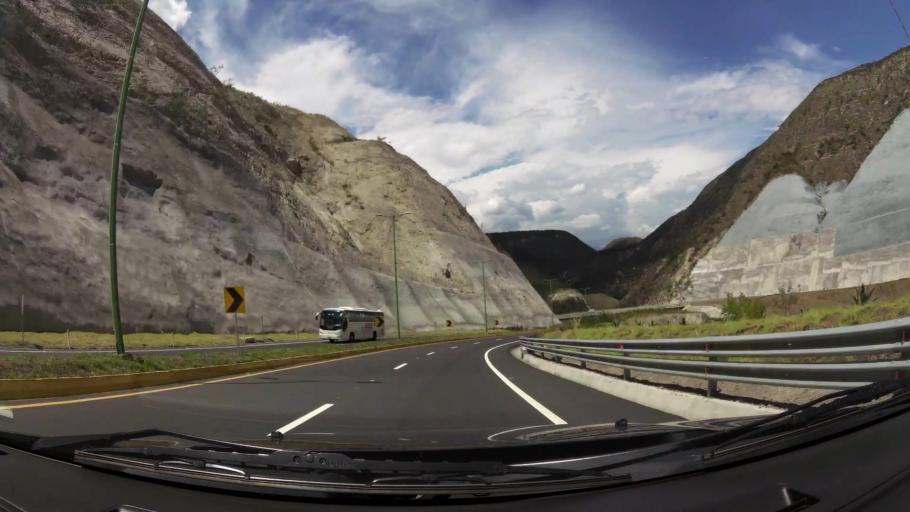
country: EC
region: Pichincha
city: Quito
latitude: -0.1019
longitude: -78.3844
